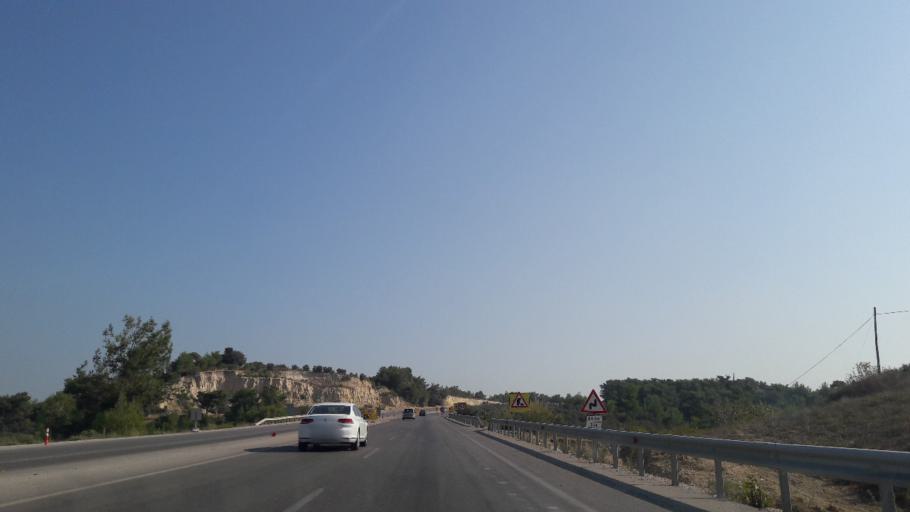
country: TR
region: Adana
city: Yuregir
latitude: 37.0779
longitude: 35.4725
